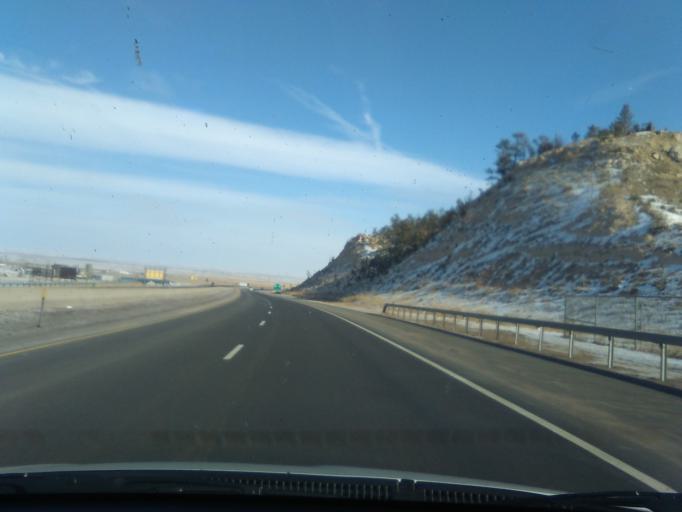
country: US
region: Wyoming
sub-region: Laramie County
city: Pine Bluffs
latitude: 41.1764
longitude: -104.0595
